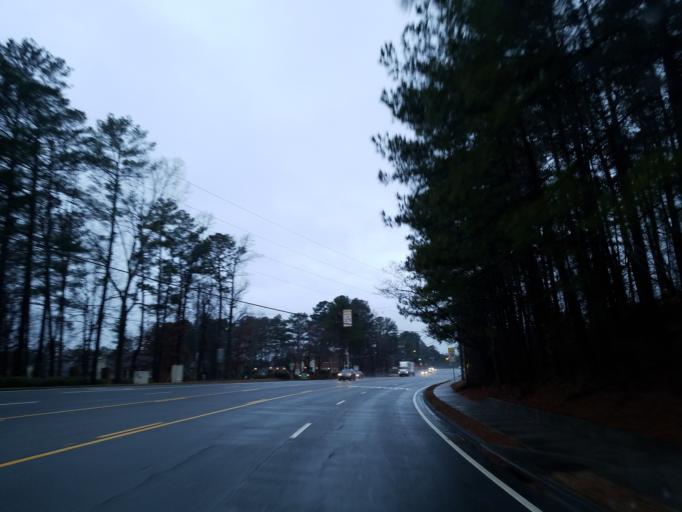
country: US
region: Georgia
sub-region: DeKalb County
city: Dunwoody
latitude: 33.9923
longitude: -84.2796
